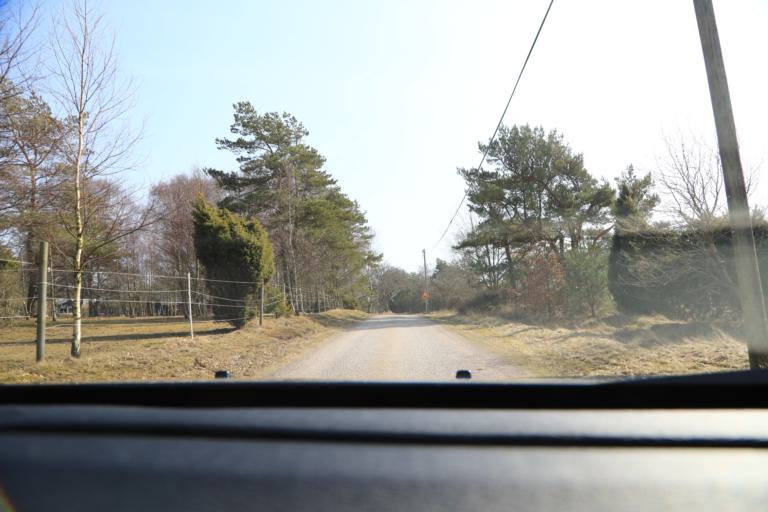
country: SE
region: Halland
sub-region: Kungsbacka Kommun
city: Frillesas
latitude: 57.2653
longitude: 12.1421
